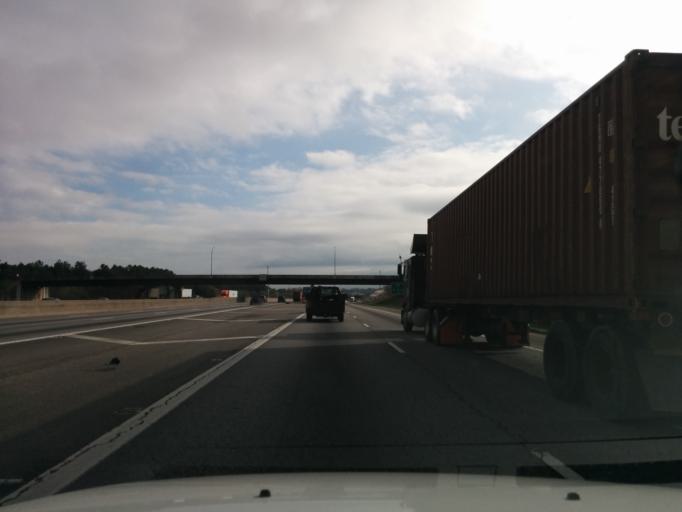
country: US
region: Georgia
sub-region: Fulton County
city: Hapeville
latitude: 33.6285
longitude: -84.4162
